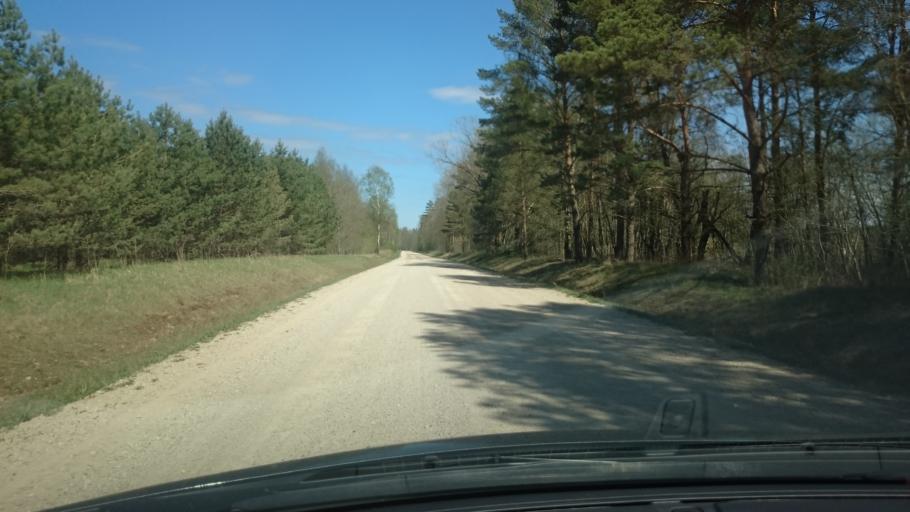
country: RU
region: Leningrad
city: Slantsy
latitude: 59.0949
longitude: 27.7891
